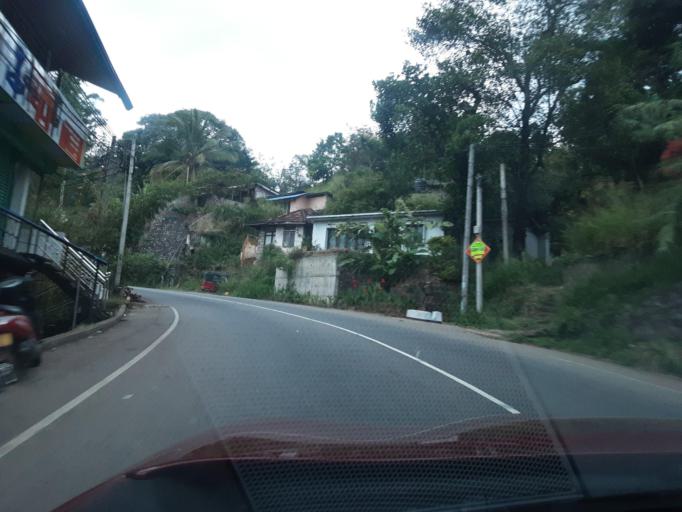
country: LK
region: Central
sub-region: Nuwara Eliya District
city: Nuwara Eliya
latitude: 6.9034
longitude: 80.9060
